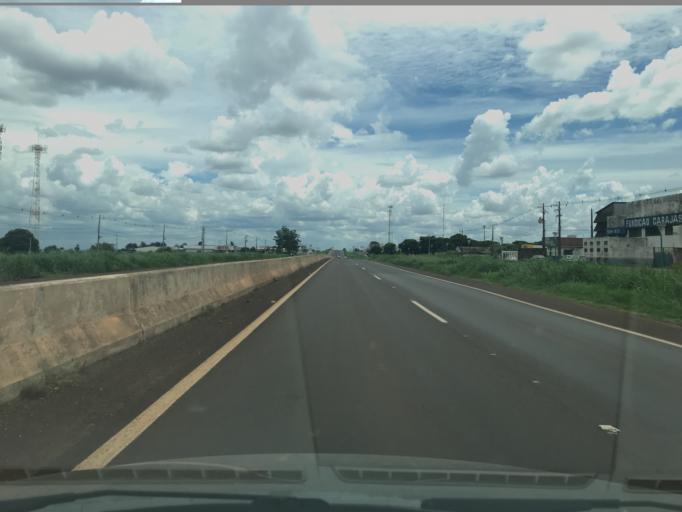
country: BR
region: Parana
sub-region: Paicandu
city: Paicandu
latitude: -23.4622
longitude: -52.0399
